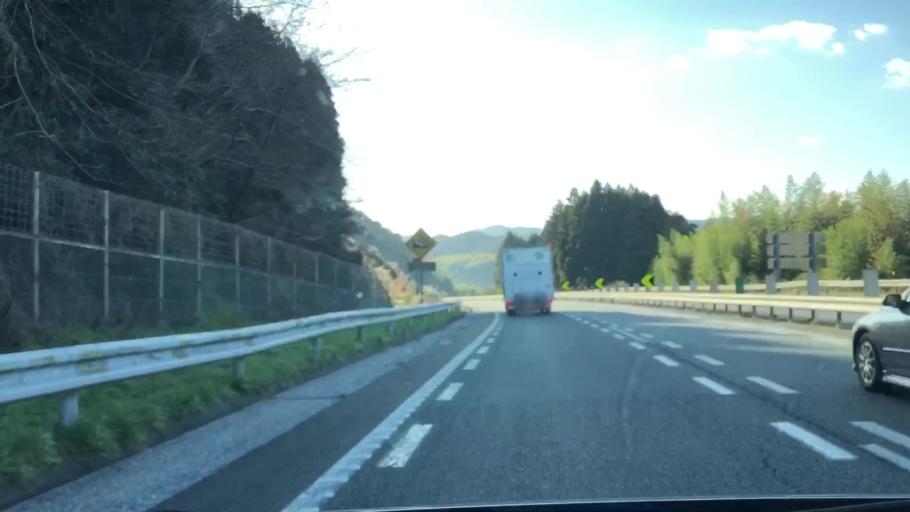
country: JP
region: Yamaguchi
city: Onoda
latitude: 34.1118
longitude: 131.1586
